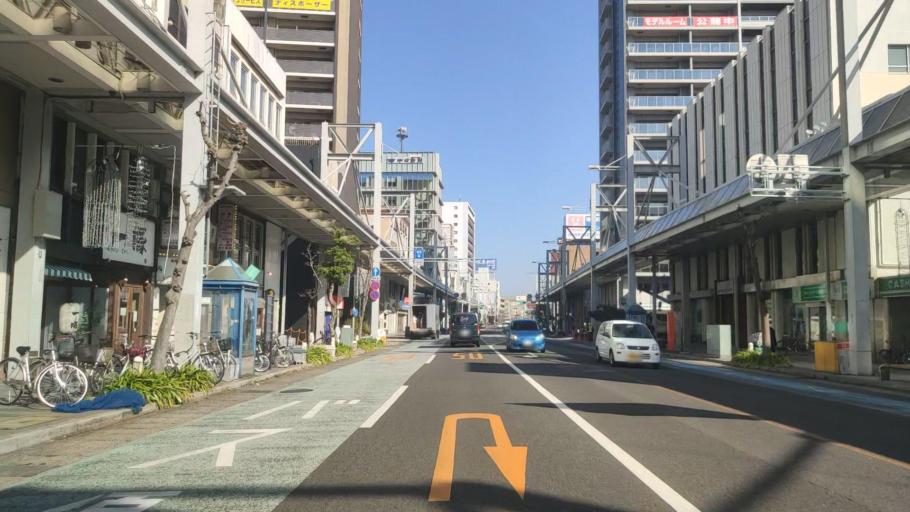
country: JP
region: Gifu
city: Gifu-shi
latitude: 35.4175
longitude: 136.7601
